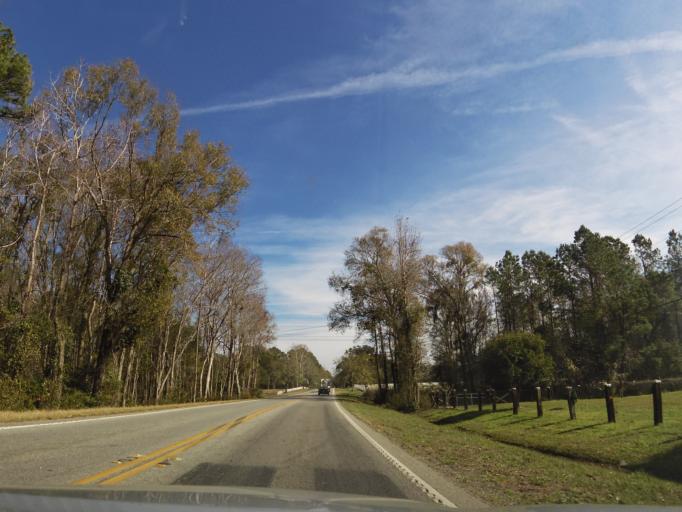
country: US
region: Georgia
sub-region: Glynn County
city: Dock Junction
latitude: 31.2744
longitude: -81.5759
